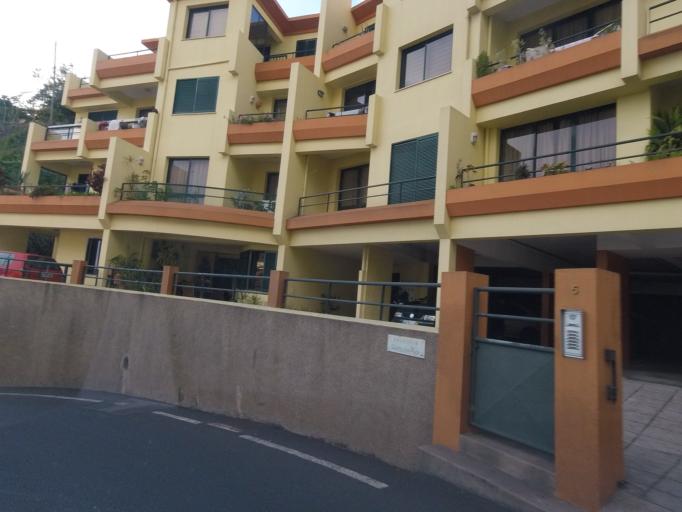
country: PT
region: Madeira
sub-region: Funchal
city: Nossa Senhora do Monte
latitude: 32.6614
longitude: -16.9023
